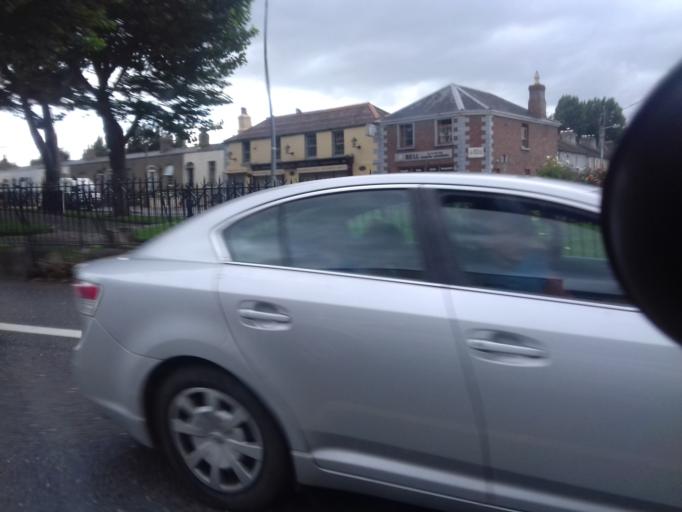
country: IE
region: Leinster
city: Rathgar
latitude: 53.3259
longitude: -6.2783
